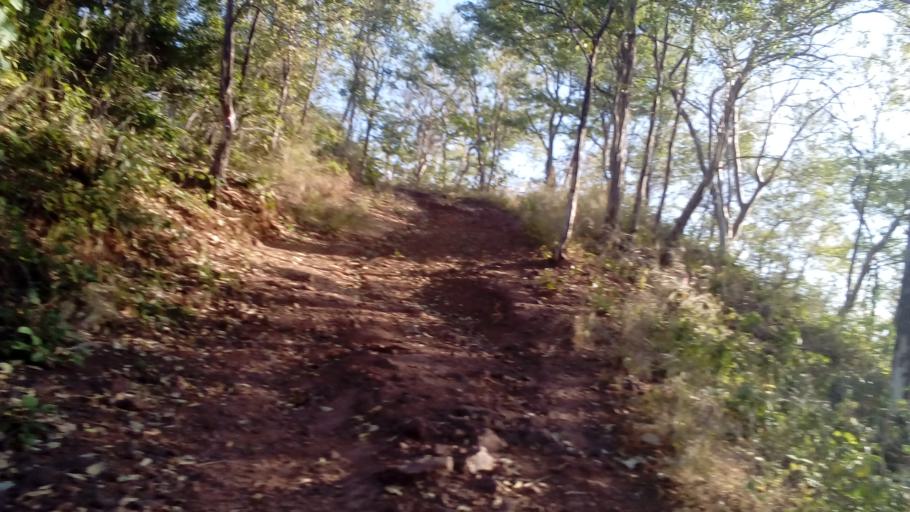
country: CR
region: Guanacaste
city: Sardinal
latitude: 10.3970
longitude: -85.8340
